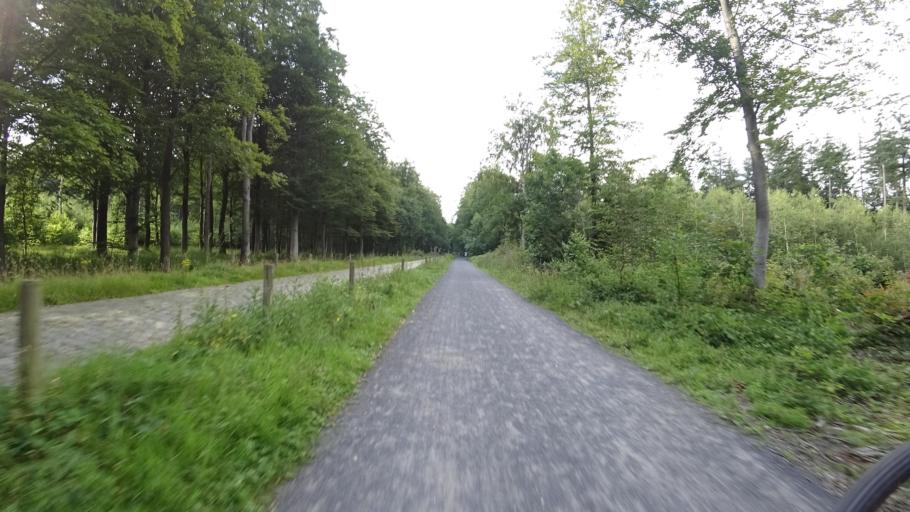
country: BE
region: Flanders
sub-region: Provincie West-Vlaanderen
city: Sint-Kruis
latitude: 51.1997
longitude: 3.2944
